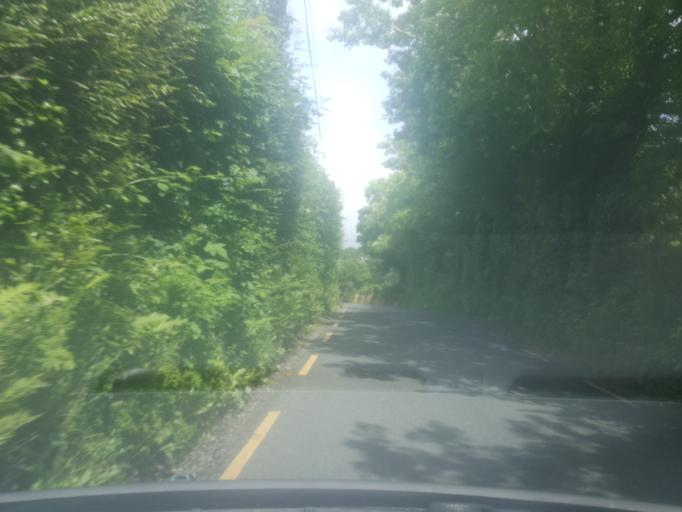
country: IE
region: Munster
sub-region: Ciarrai
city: Cill Airne
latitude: 52.0901
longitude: -9.4805
